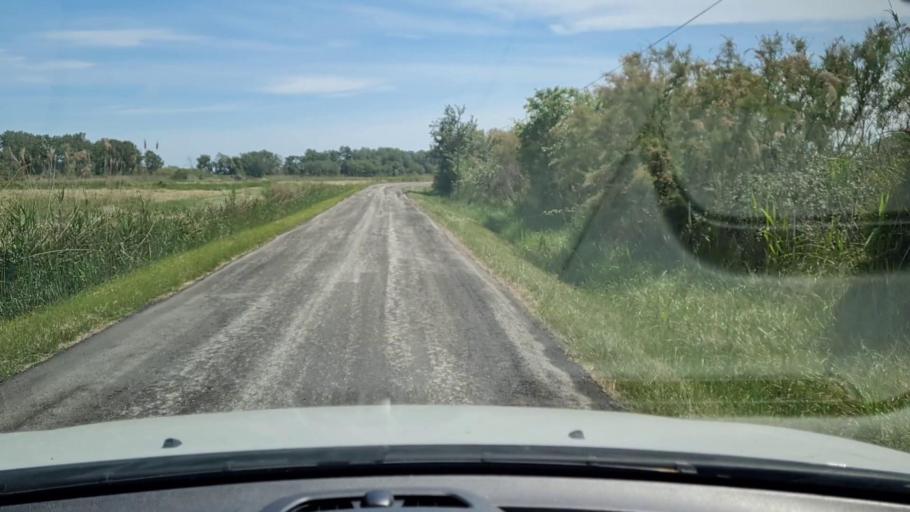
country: FR
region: Provence-Alpes-Cote d'Azur
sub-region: Departement des Bouches-du-Rhone
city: Saintes-Maries-de-la-Mer
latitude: 43.5599
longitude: 4.3821
